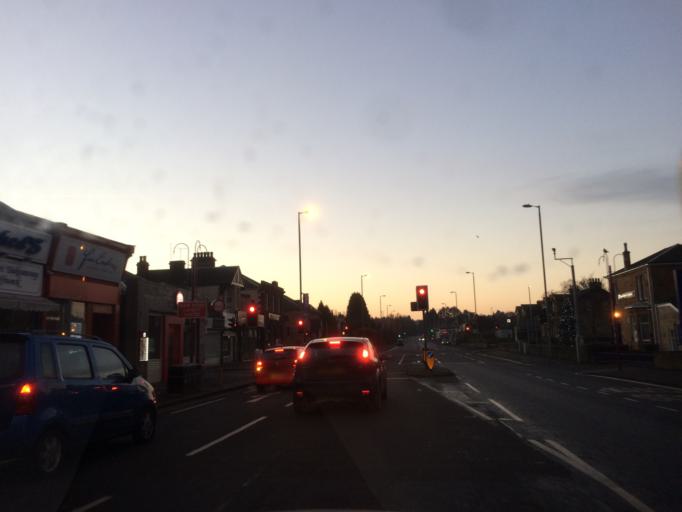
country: GB
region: Scotland
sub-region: East Renfrewshire
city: Giffnock
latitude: 55.8045
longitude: -4.2947
